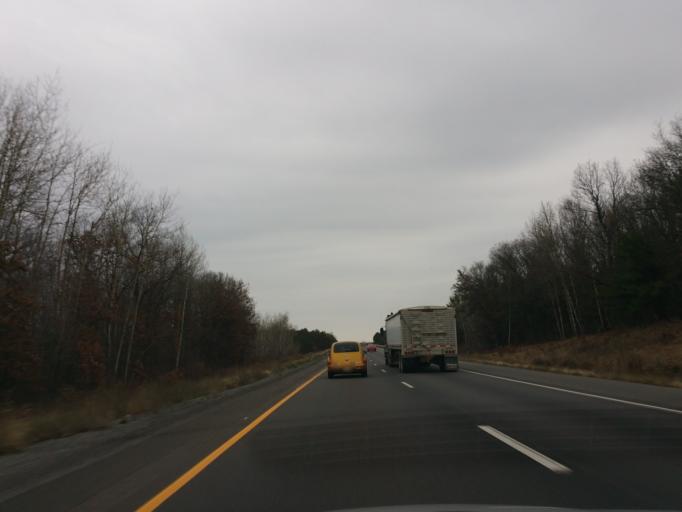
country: US
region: Wisconsin
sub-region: Jackson County
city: Black River Falls
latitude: 44.2362
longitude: -90.7161
